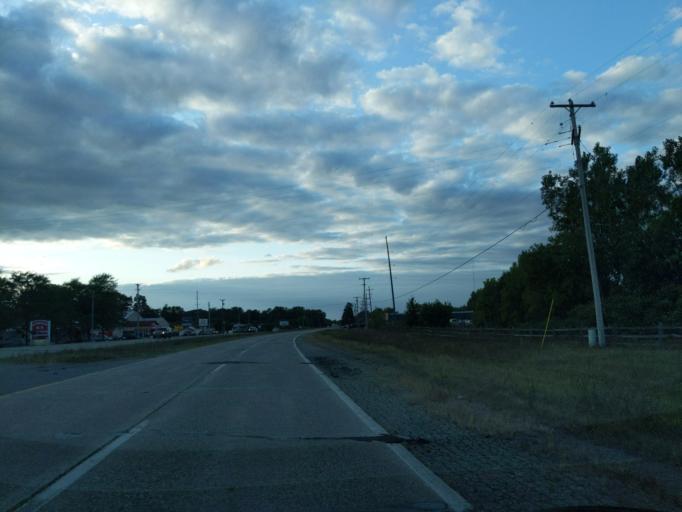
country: US
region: Michigan
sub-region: Ingham County
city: Holt
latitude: 42.6165
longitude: -84.4968
